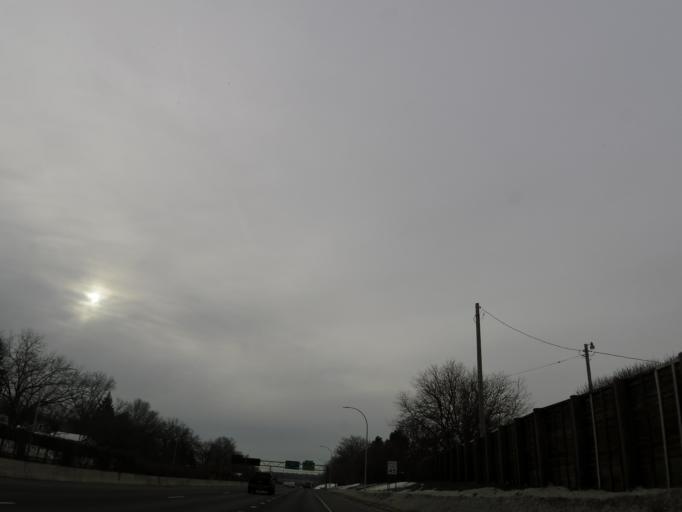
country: US
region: Minnesota
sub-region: Dakota County
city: Mendota Heights
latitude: 44.9200
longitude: -93.1444
